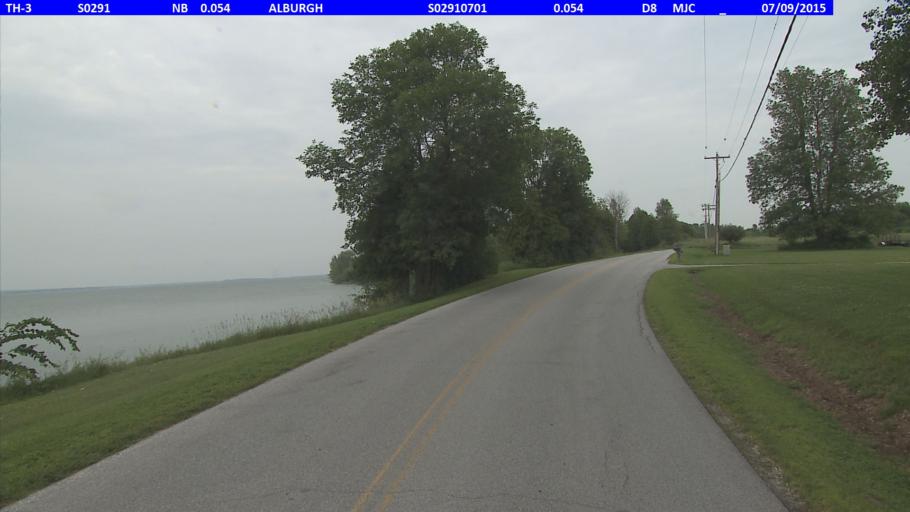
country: US
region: Vermont
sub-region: Grand Isle County
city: North Hero
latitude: 44.9055
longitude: -73.3135
